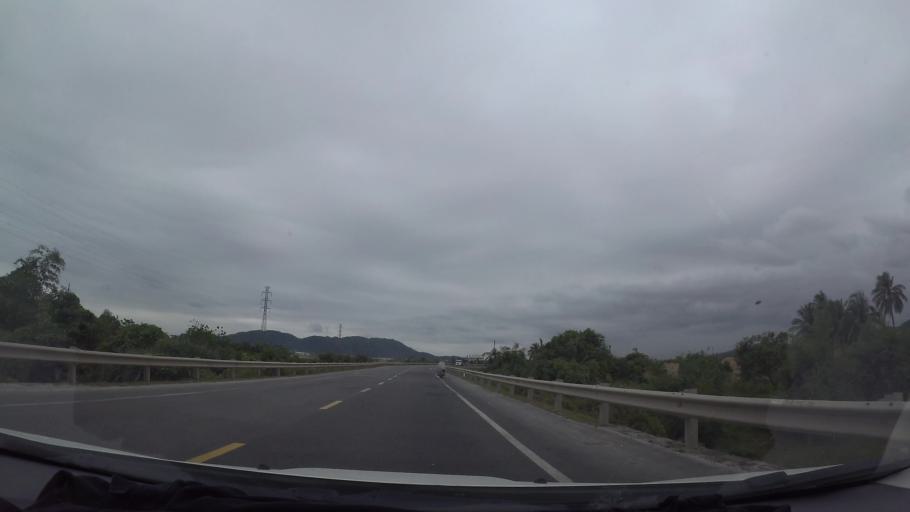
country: VN
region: Da Nang
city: Lien Chieu
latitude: 16.1108
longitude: 108.1049
